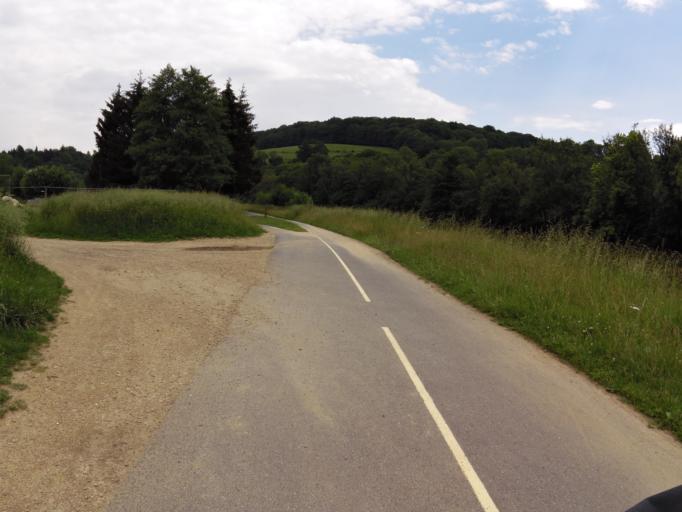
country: FR
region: Champagne-Ardenne
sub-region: Departement des Ardennes
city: Montcy-Notre-Dame
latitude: 49.7706
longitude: 4.7437
